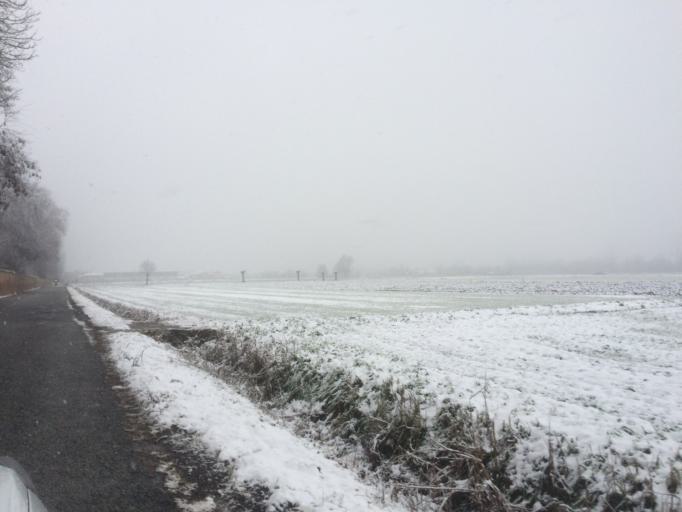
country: IT
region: Piedmont
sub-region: Provincia di Cuneo
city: Racconigi
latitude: 44.7752
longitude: 7.6701
